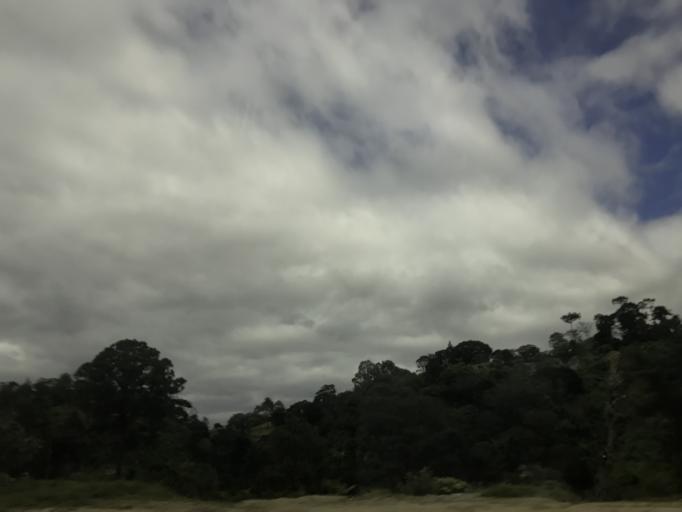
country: GT
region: Chimaltenango
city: Parramos
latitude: 14.6251
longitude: -90.8026
